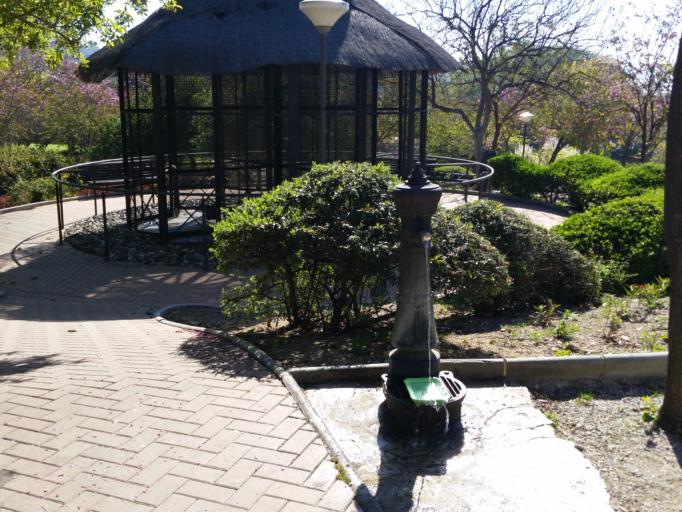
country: ES
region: Andalusia
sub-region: Provincia de Malaga
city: Torremolinos
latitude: 36.5934
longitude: -4.5291
